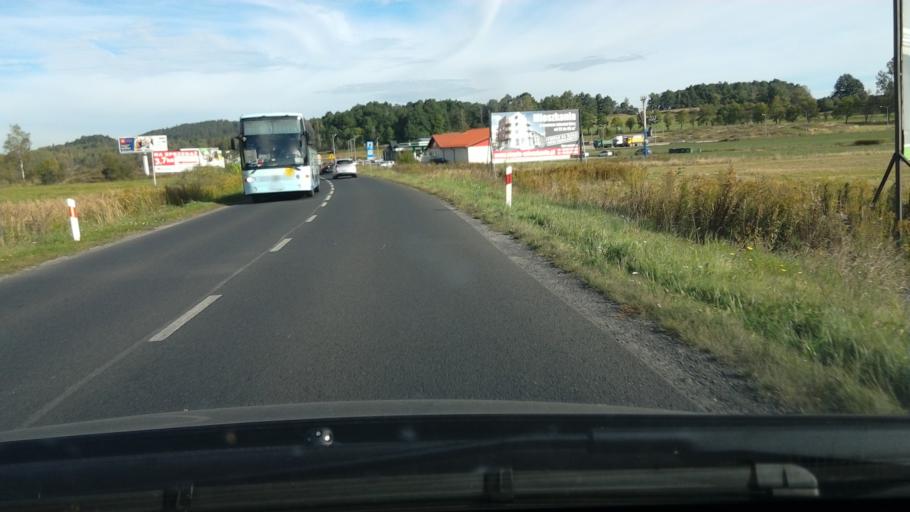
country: PL
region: Lower Silesian Voivodeship
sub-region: Powiat jeleniogorski
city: Myslakowice
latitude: 50.8552
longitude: 15.7746
